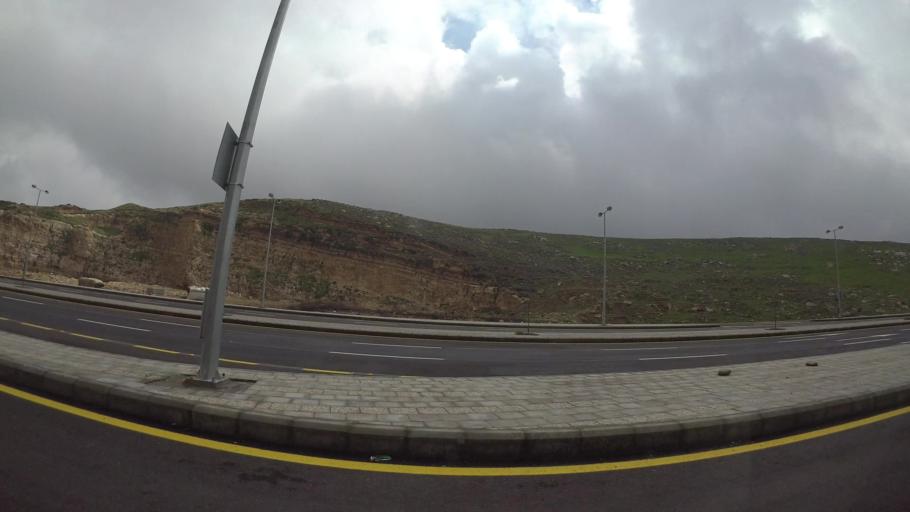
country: JO
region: Amman
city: Al Bunayyat ash Shamaliyah
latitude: 31.9340
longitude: 35.8702
